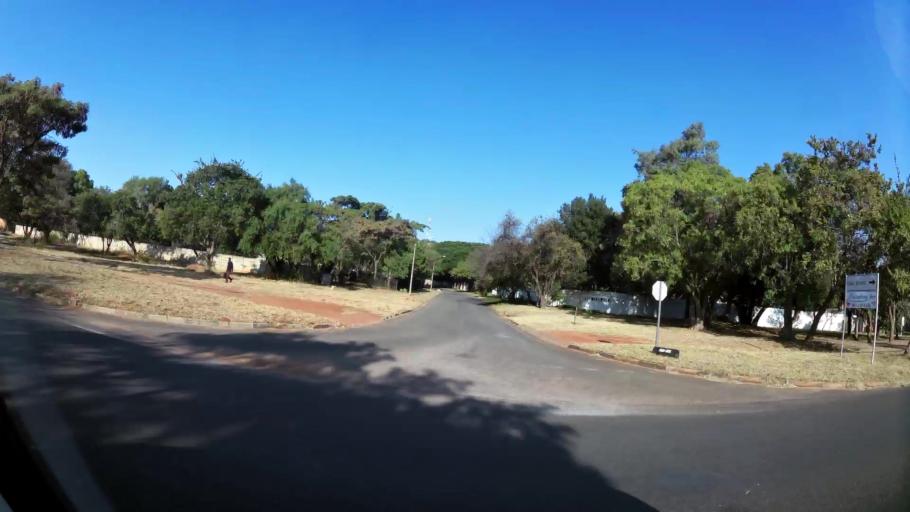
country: ZA
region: North-West
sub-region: Bojanala Platinum District Municipality
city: Rustenburg
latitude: -25.6870
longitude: 27.2386
